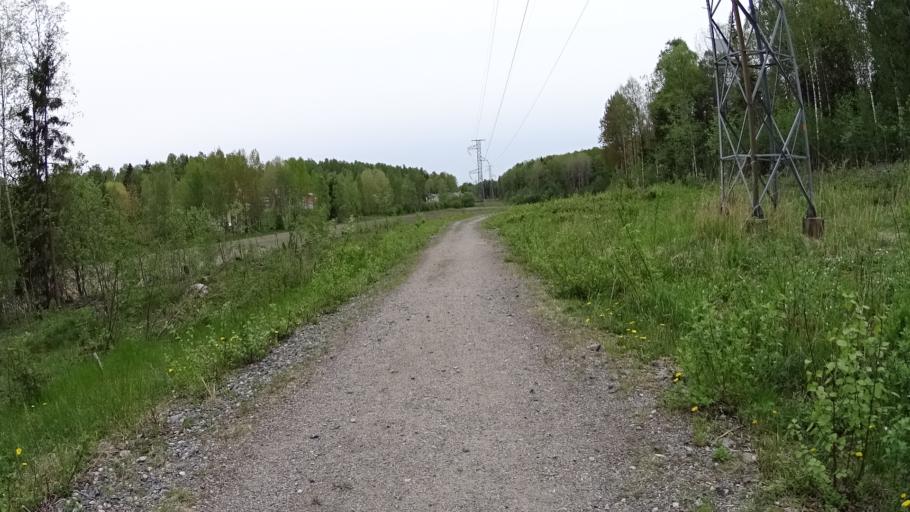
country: FI
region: Uusimaa
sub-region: Helsinki
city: Kilo
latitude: 60.2498
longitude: 24.7988
